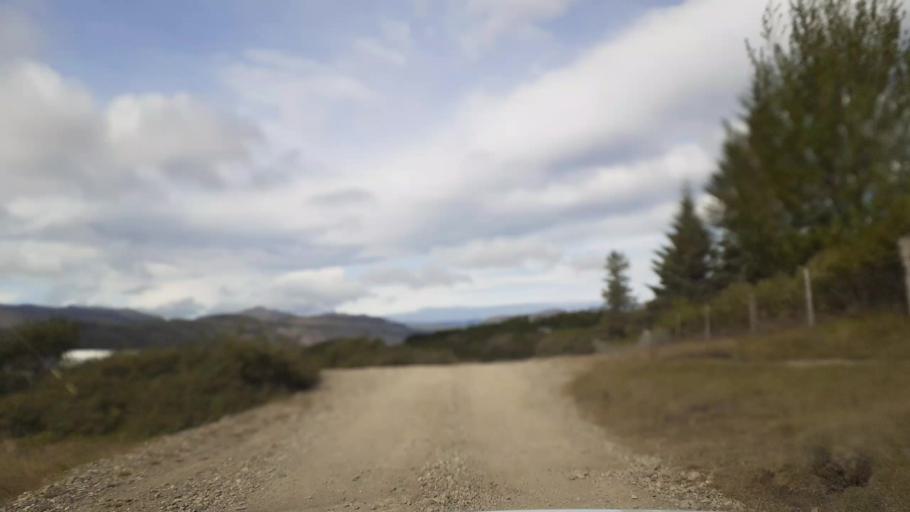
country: IS
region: East
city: Hoefn
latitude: 64.4352
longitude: -14.8976
